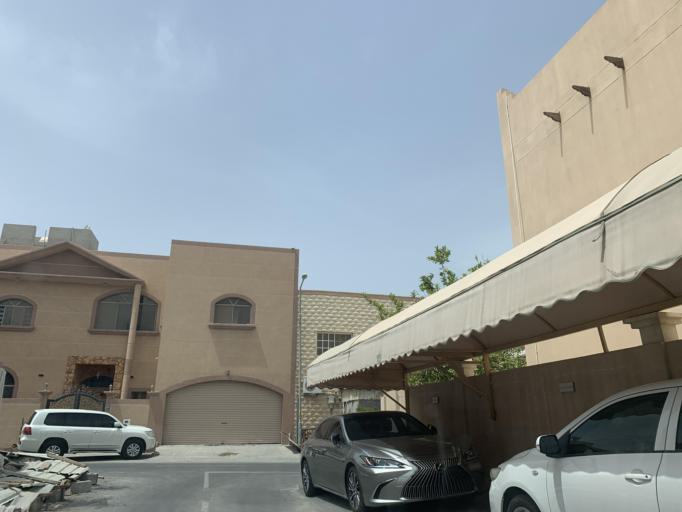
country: BH
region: Northern
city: Ar Rifa'
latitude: 26.1355
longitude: 50.5633
